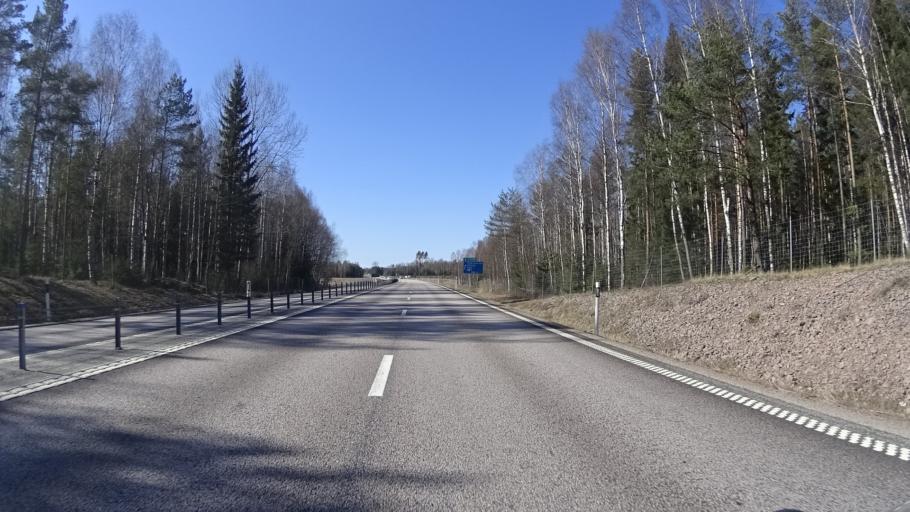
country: SE
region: Vaermland
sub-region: Karlstads Kommun
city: Skattkarr
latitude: 59.3860
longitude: 13.8710
